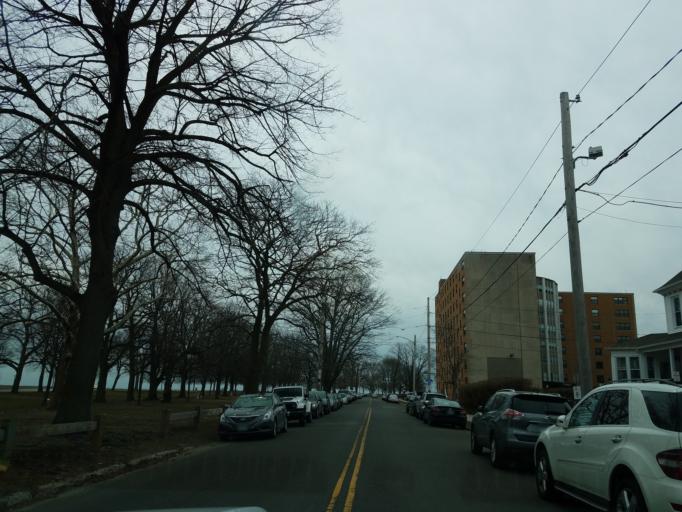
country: US
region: Connecticut
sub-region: Fairfield County
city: Bridgeport
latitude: 41.1654
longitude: -73.1862
